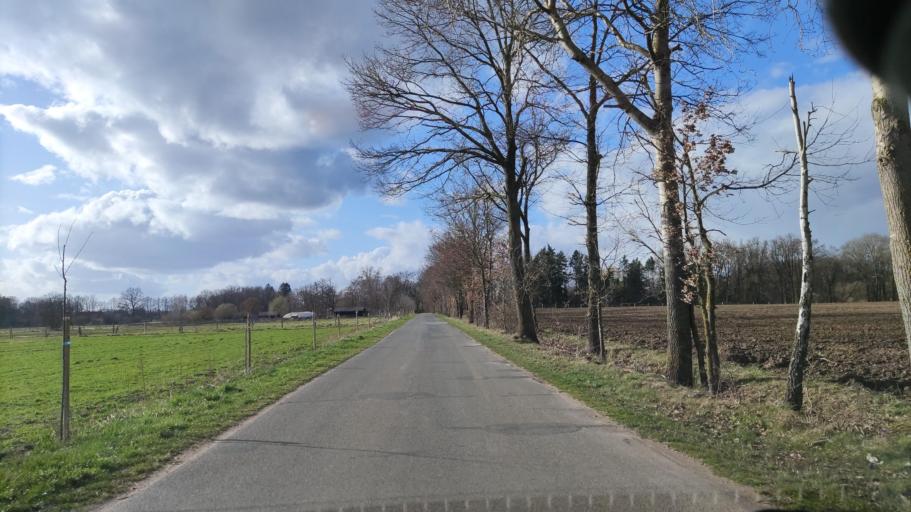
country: DE
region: Lower Saxony
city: Jelmstorf
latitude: 53.1289
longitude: 10.5177
